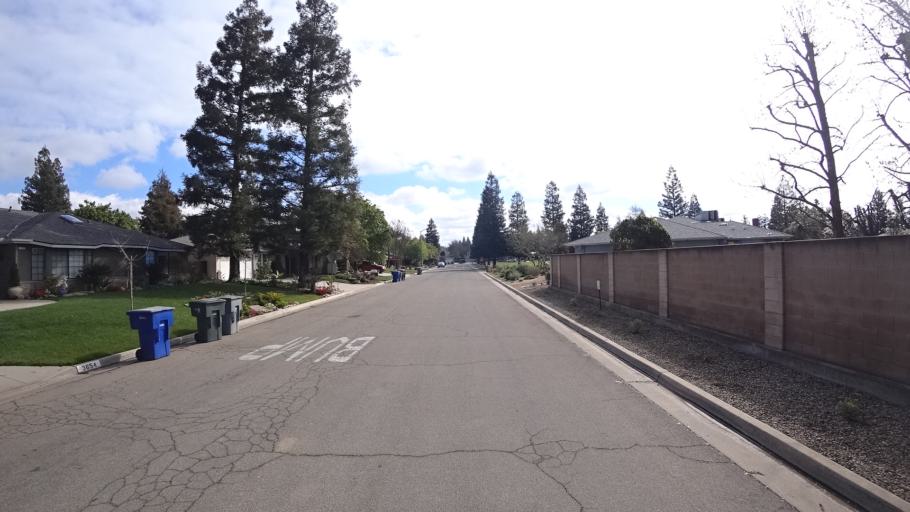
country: US
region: California
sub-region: Fresno County
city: Fresno
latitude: 36.8328
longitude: -119.8594
